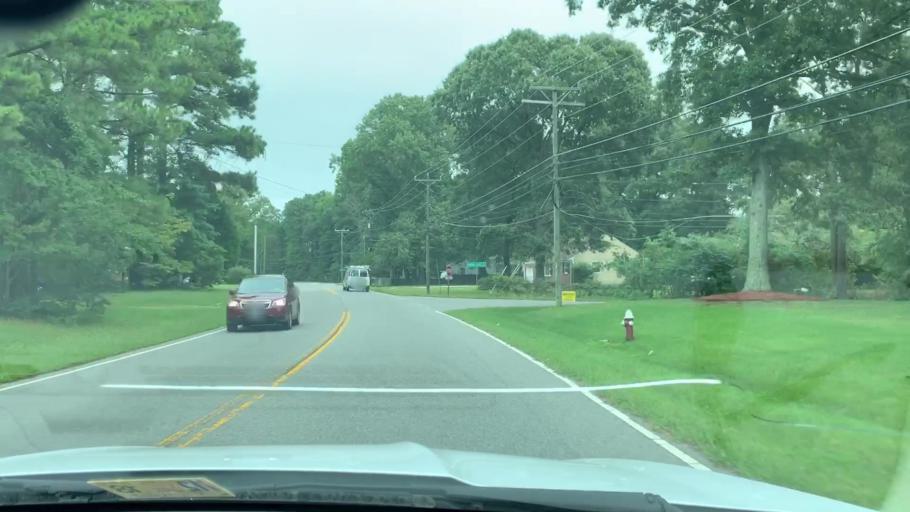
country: US
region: Virginia
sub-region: York County
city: Yorktown
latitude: 37.1873
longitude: -76.4382
